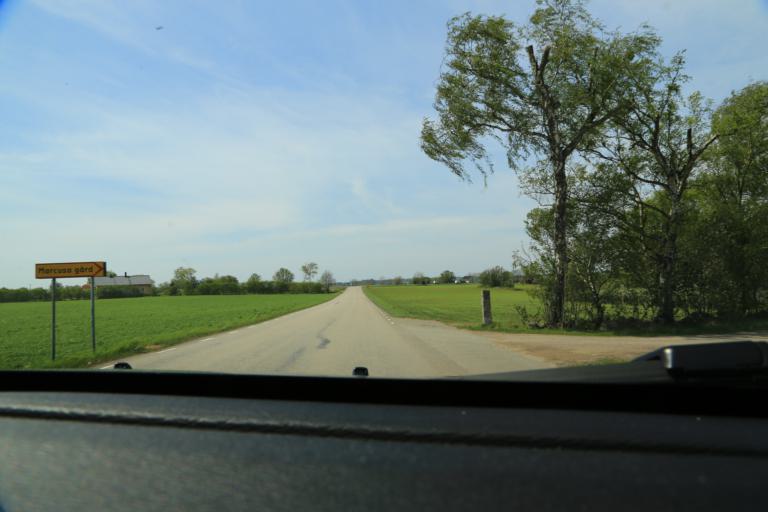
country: SE
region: Halland
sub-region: Varbergs Kommun
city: Tvaaker
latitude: 57.0998
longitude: 12.3492
